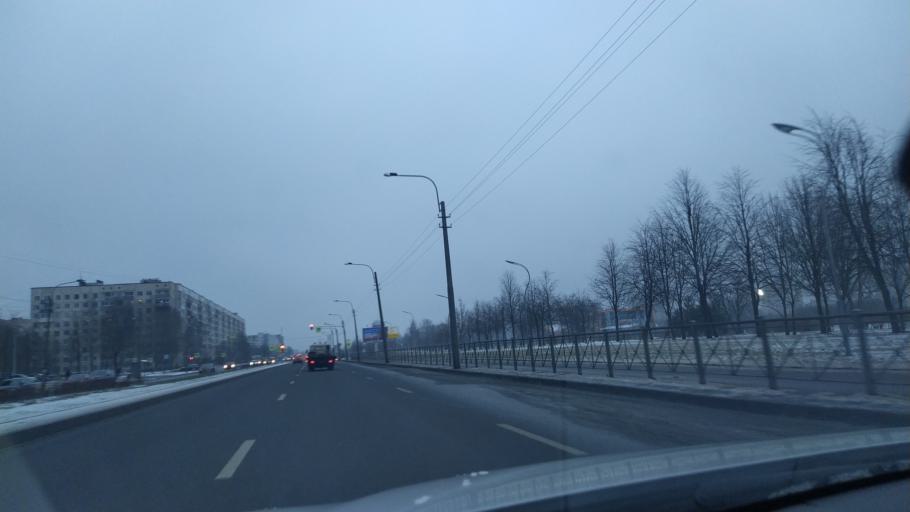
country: RU
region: St.-Petersburg
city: Grazhdanka
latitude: 60.0283
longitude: 30.4008
